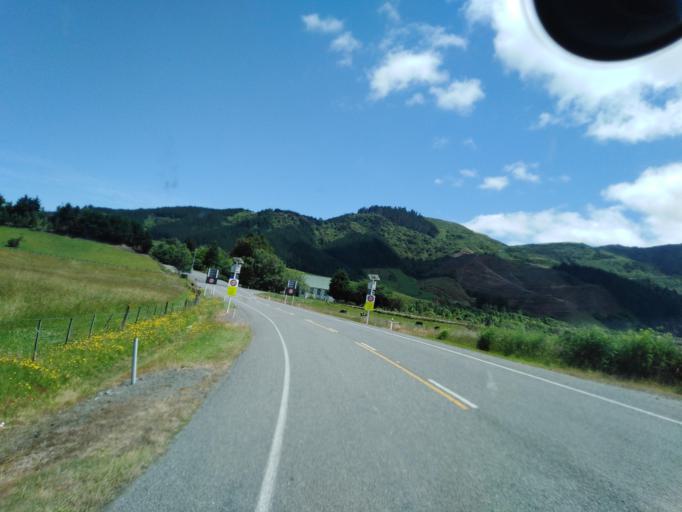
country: NZ
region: Nelson
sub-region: Nelson City
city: Nelson
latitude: -41.2120
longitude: 173.3956
